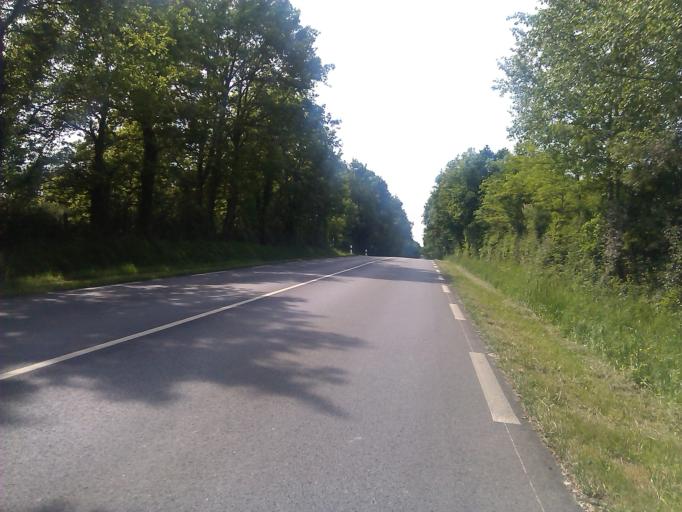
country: FR
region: Centre
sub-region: Departement de l'Indre
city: La Chatre
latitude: 46.5576
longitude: 2.0662
